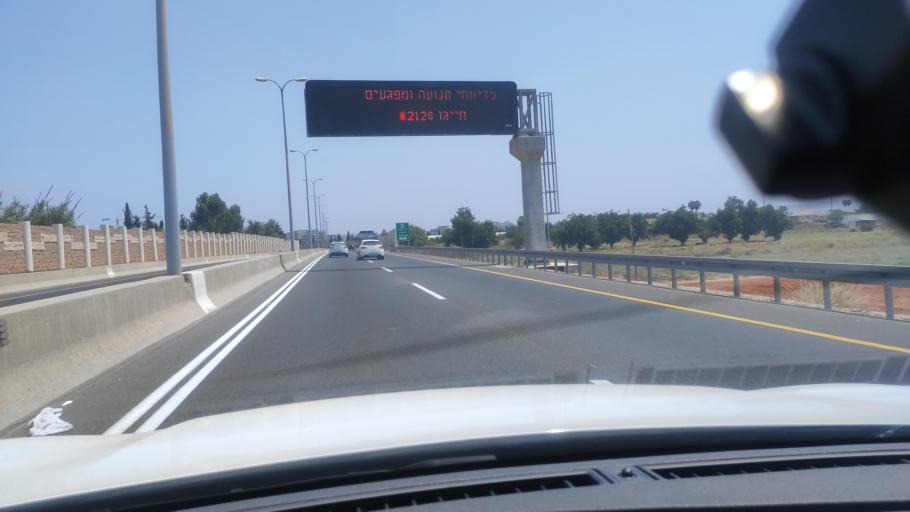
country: IL
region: Central District
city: Kfar Saba
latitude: 32.1549
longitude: 34.9240
